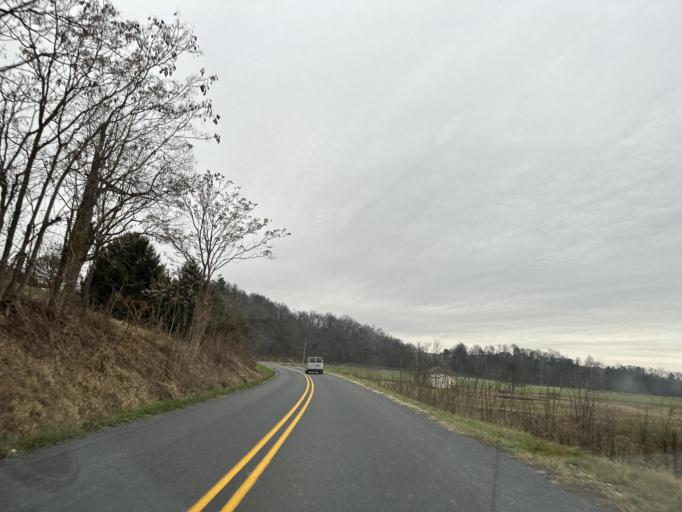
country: US
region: Virginia
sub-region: Rockingham County
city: Bridgewater
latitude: 38.3947
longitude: -79.0496
